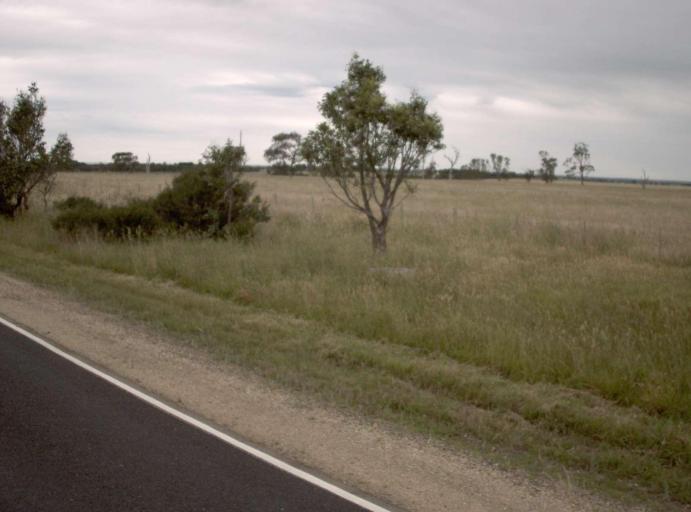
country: AU
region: Victoria
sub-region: Wellington
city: Sale
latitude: -37.9980
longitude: 147.2129
